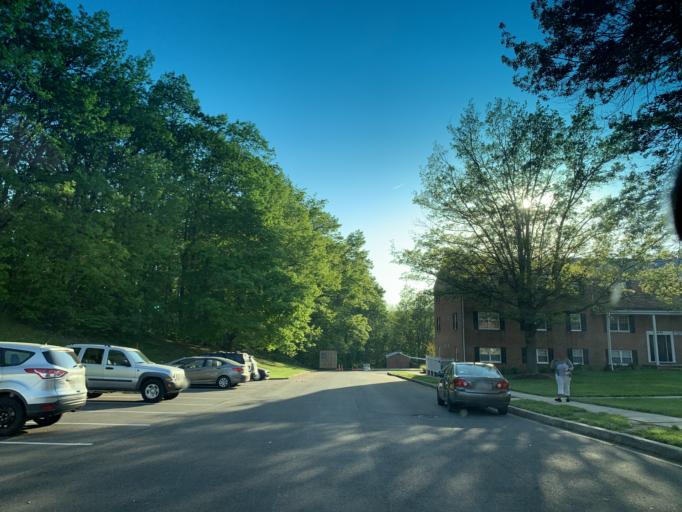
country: US
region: Maryland
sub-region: Harford County
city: Aberdeen
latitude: 39.5237
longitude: -76.1925
